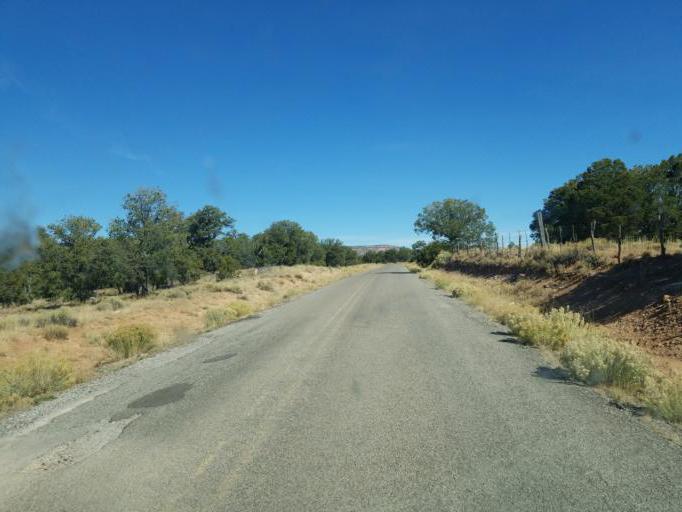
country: US
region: New Mexico
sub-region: McKinley County
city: Thoreau
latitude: 35.4210
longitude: -108.2861
